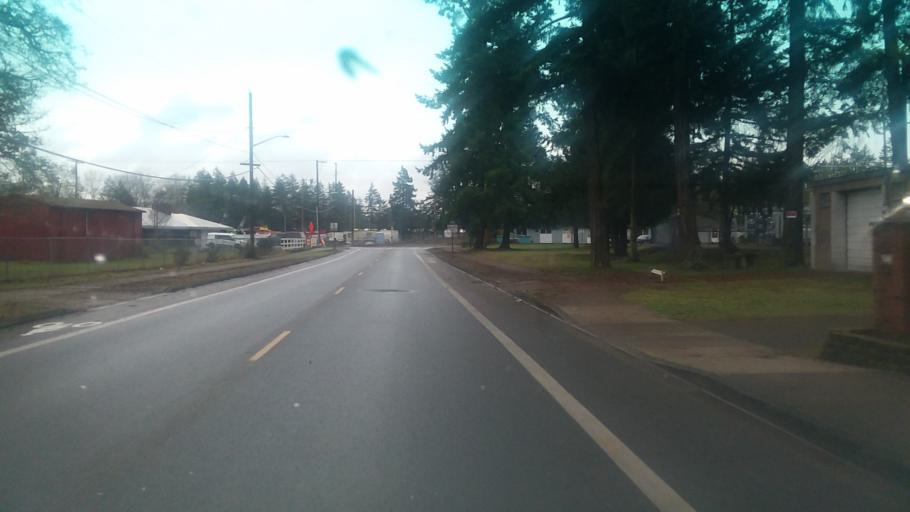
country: US
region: Washington
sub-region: Pierce County
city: Fort Lewis
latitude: 47.1272
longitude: -122.5466
